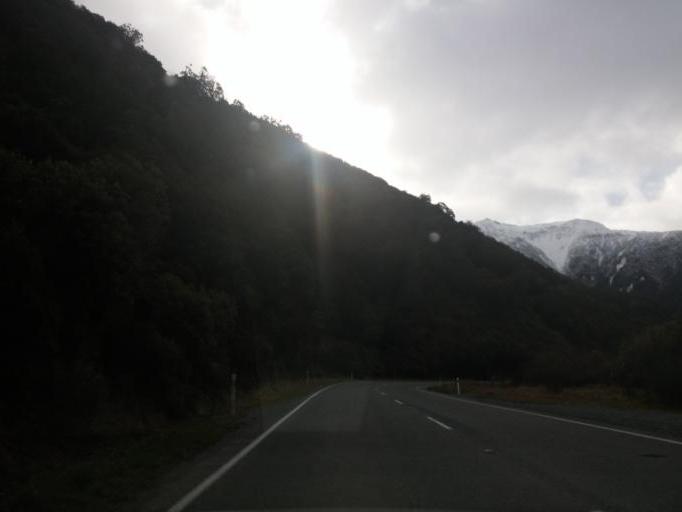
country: NZ
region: West Coast
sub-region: Grey District
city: Greymouth
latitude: -42.8218
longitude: 171.5632
